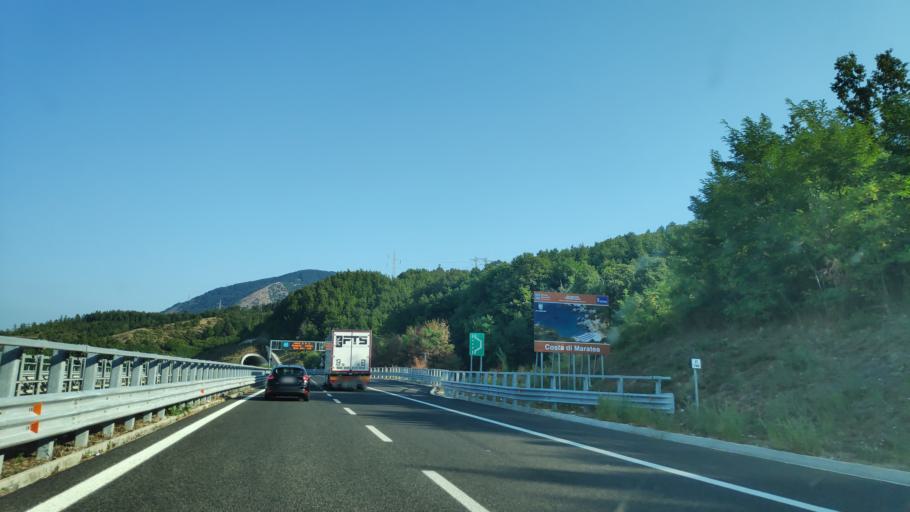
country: IT
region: Basilicate
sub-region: Provincia di Potenza
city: Nemoli
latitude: 40.1063
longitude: 15.7950
